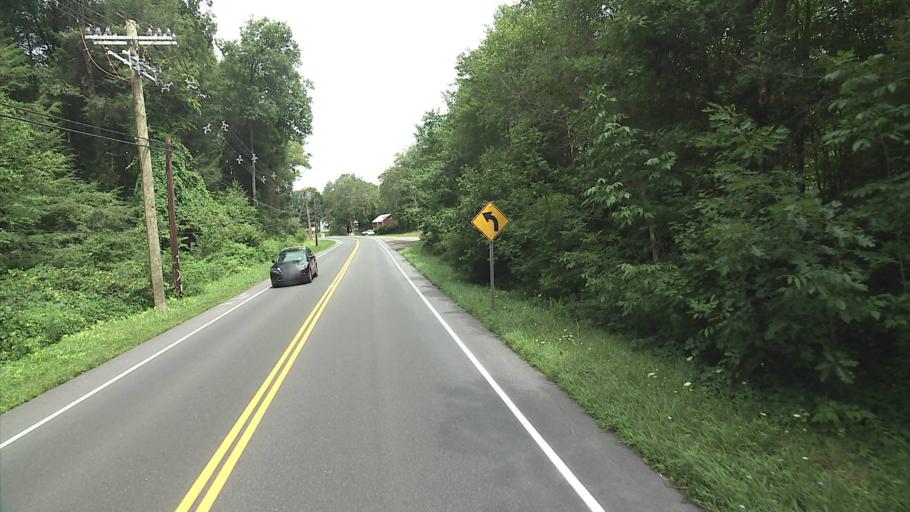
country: US
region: Connecticut
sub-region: New Haven County
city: Heritage Village
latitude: 41.5059
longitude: -73.2375
